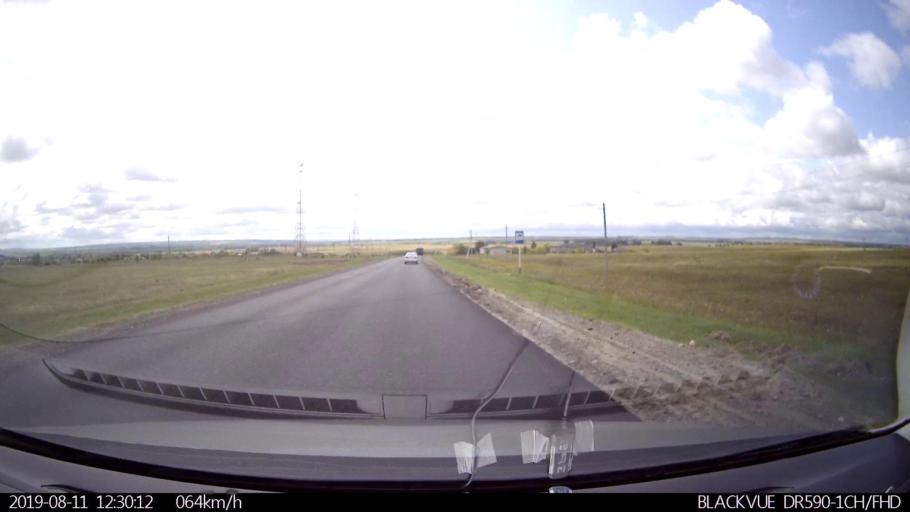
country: RU
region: Ulyanovsk
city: Ignatovka
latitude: 53.8279
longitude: 47.8962
